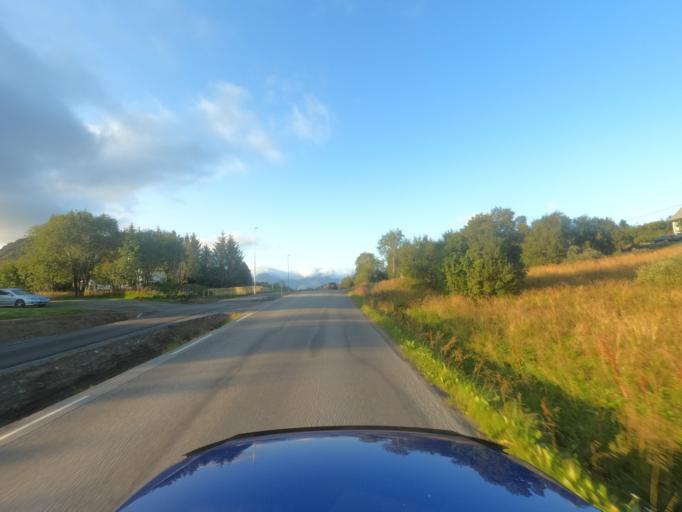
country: NO
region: Nordland
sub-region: Vestvagoy
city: Gravdal
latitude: 68.1031
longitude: 13.5490
